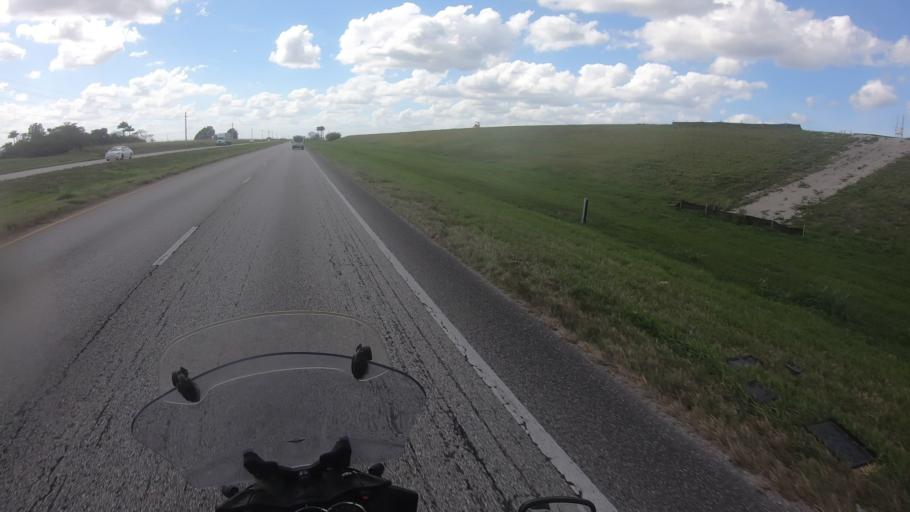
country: US
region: Florida
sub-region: Palm Beach County
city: South Bay
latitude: 26.6792
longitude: -80.7414
